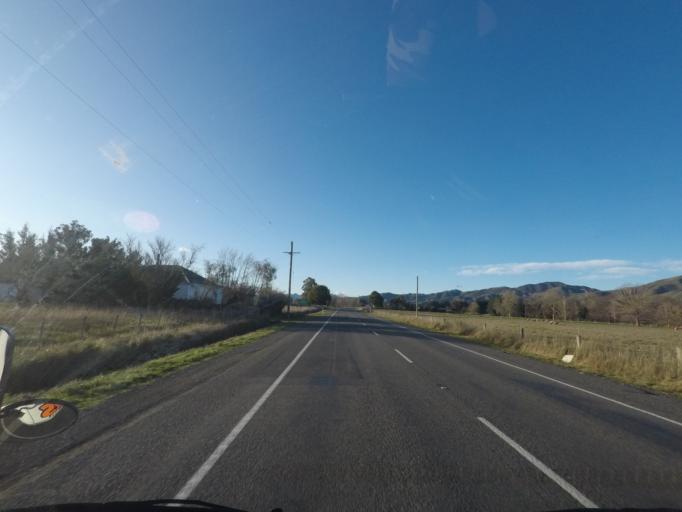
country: NZ
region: Canterbury
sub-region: Kaikoura District
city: Kaikoura
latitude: -42.7126
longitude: 173.2911
